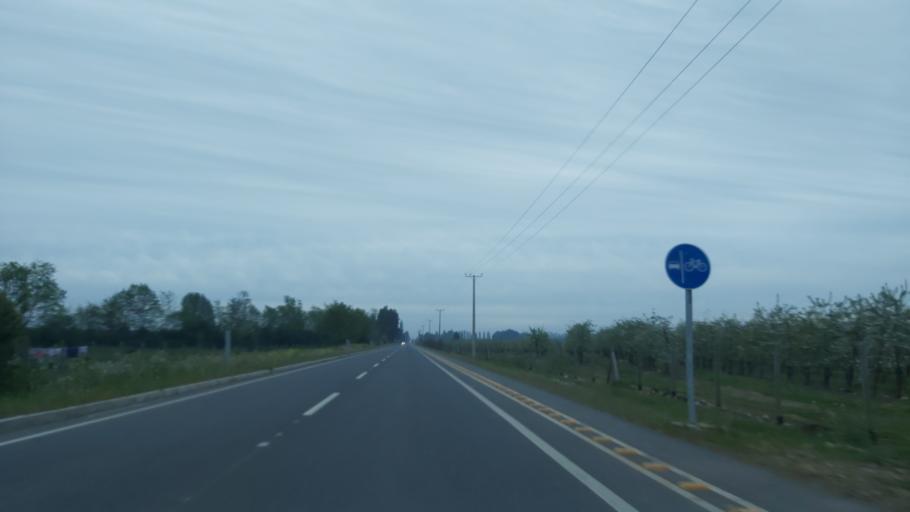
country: CL
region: Maule
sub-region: Provincia de Linares
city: Colbun
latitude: -35.6780
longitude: -71.4699
